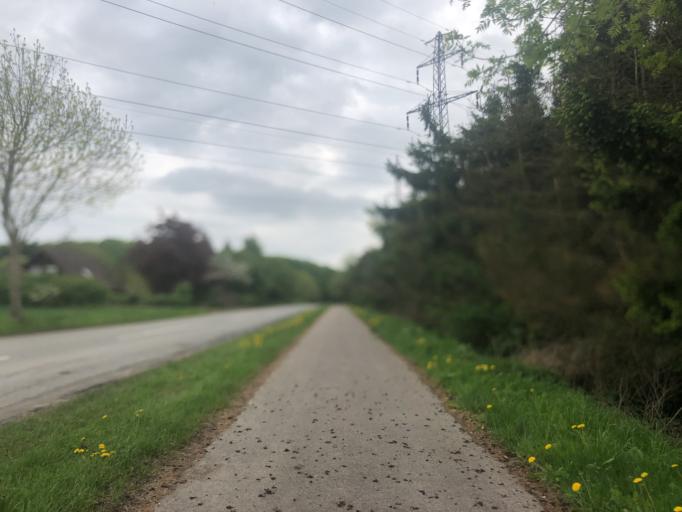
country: DK
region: Zealand
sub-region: Koge Kommune
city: Bjaeverskov
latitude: 55.4468
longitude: 12.0417
